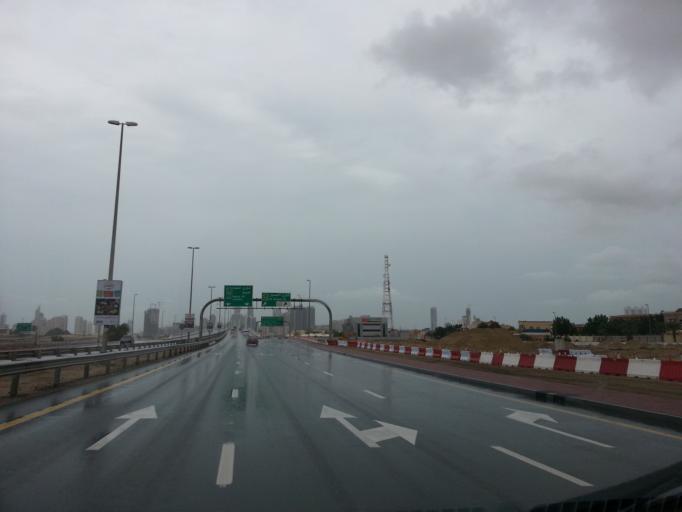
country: AE
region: Dubai
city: Dubai
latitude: 25.0826
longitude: 55.2022
